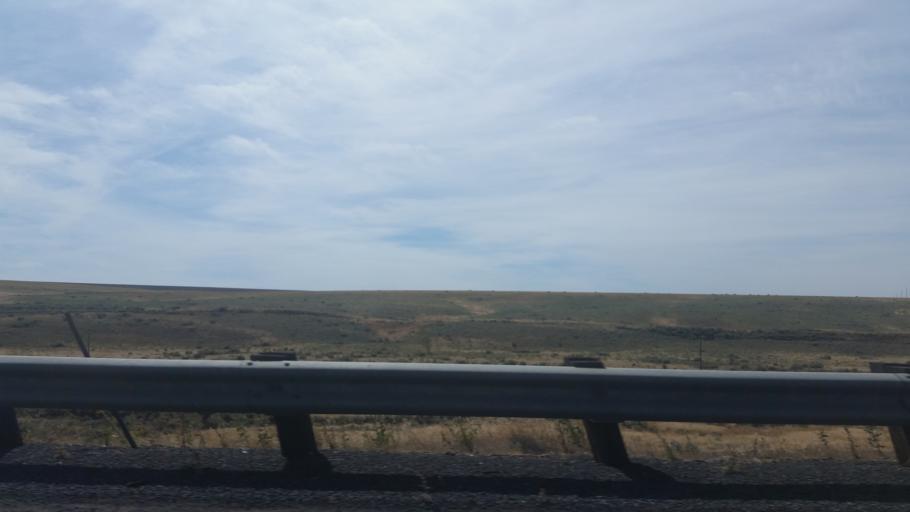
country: US
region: Washington
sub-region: Adams County
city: Ritzville
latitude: 47.1016
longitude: -118.6002
